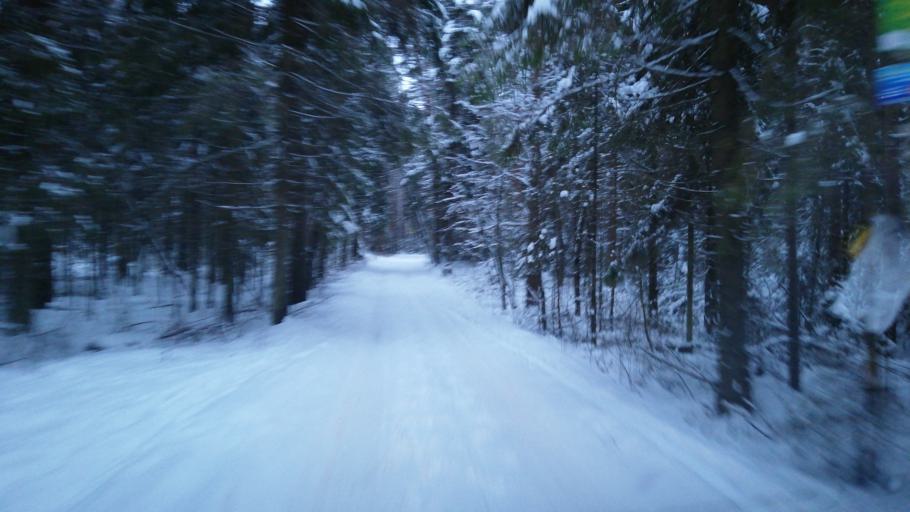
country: RU
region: Jaroslavl
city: Krasnyye Tkachi
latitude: 57.4488
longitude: 39.7948
